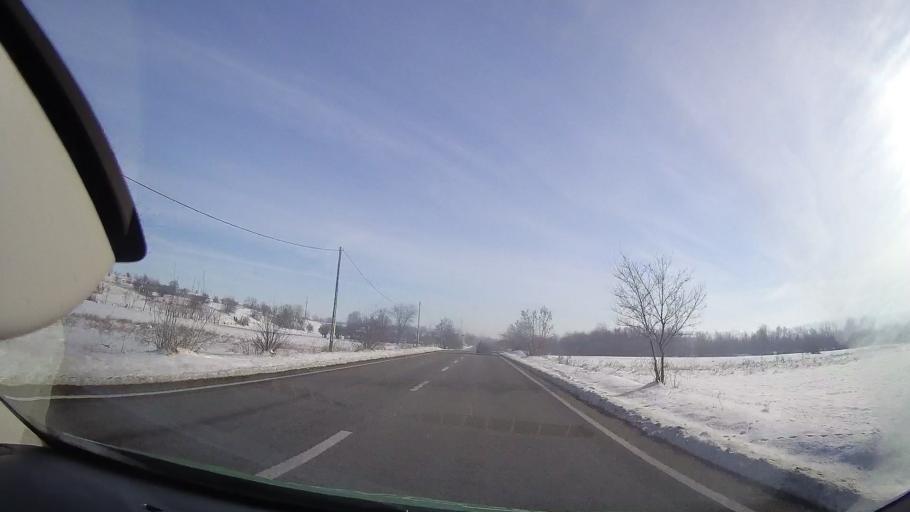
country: RO
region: Neamt
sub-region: Comuna Ghindaoani
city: Ghindaoani
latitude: 47.0767
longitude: 26.3524
